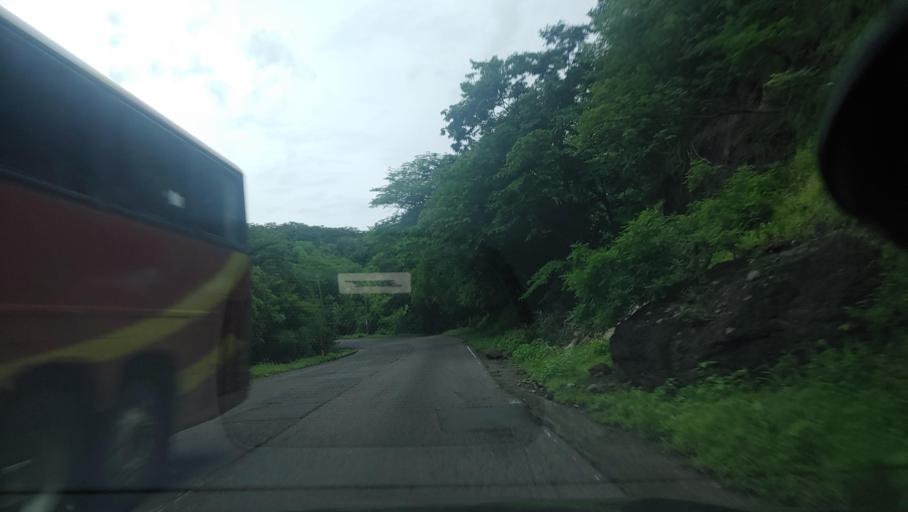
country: HN
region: Choluteca
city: Corpus
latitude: 13.3718
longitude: -87.0416
